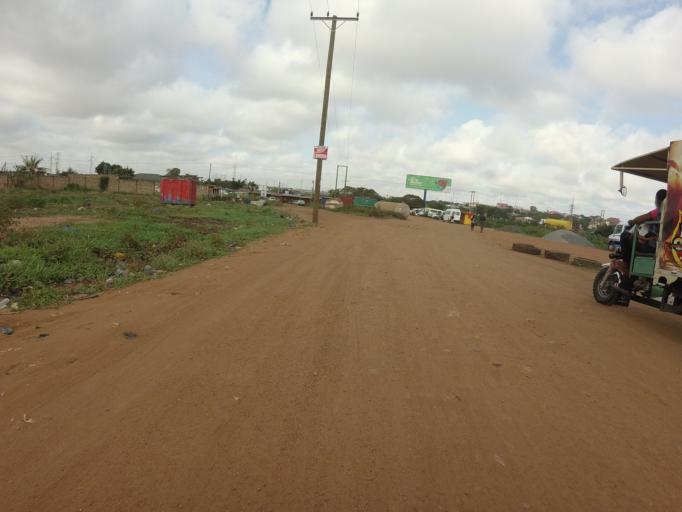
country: GH
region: Greater Accra
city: Tema
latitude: 5.6746
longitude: -0.0453
